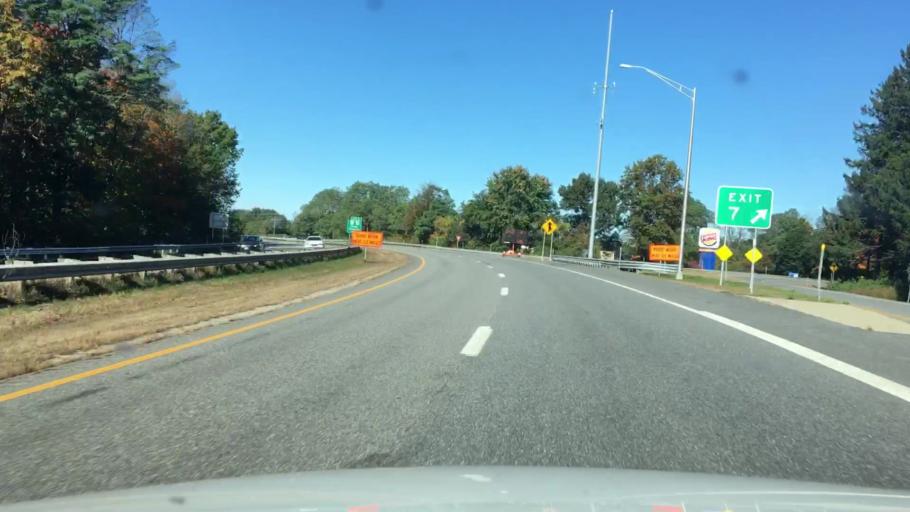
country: US
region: New Hampshire
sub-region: Strafford County
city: Dover
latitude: 43.1802
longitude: -70.8738
